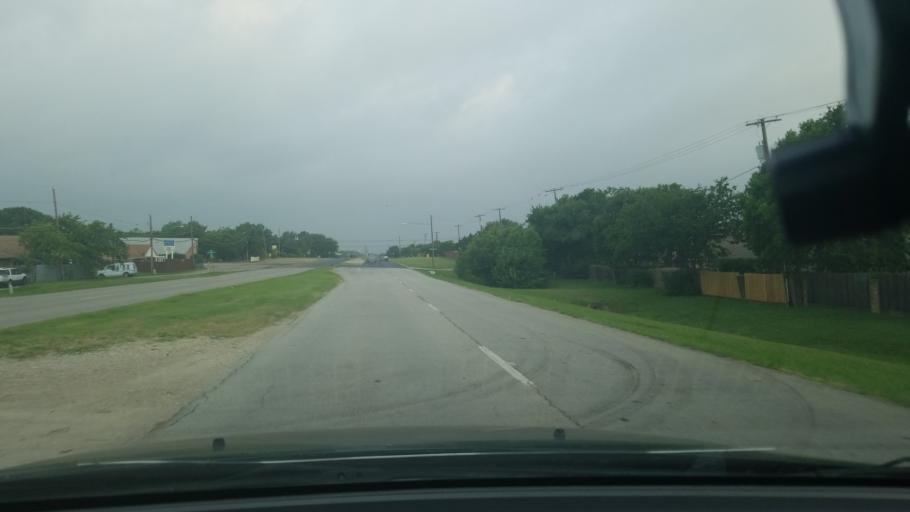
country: US
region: Texas
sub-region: Dallas County
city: Balch Springs
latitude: 32.7684
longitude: -96.6589
